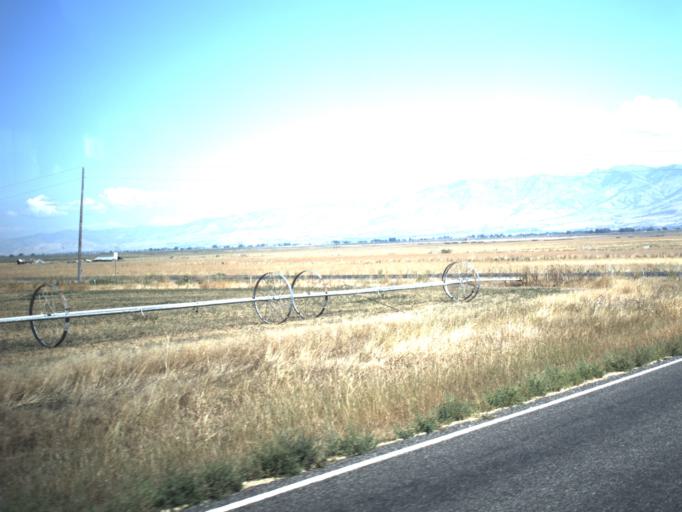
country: US
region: Utah
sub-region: Cache County
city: Benson
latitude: 41.8448
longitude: -111.9522
